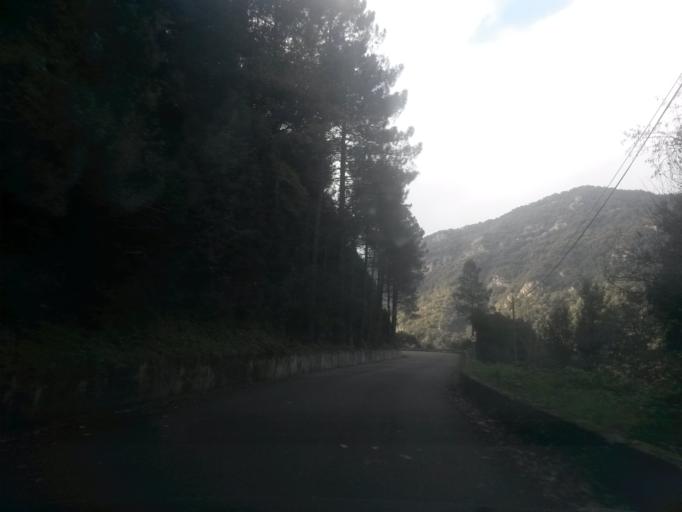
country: ES
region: Catalonia
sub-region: Provincia de Girona
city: Susqueda
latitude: 41.9827
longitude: 2.5357
